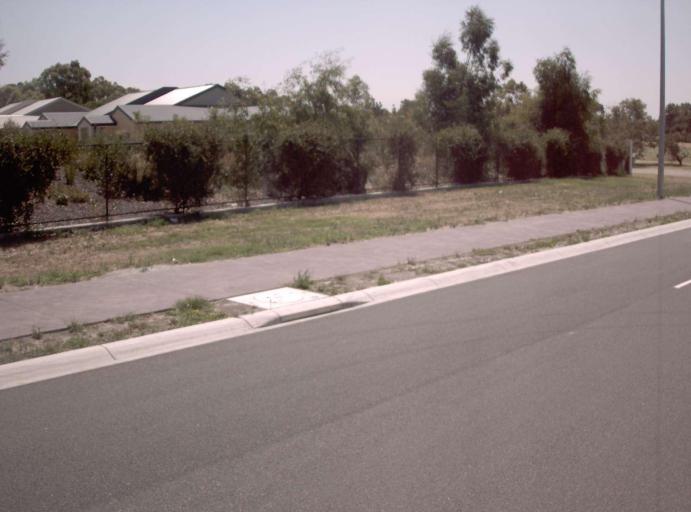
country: AU
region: Victoria
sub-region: Kingston
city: Dingley Village
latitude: -37.9855
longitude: 145.1454
